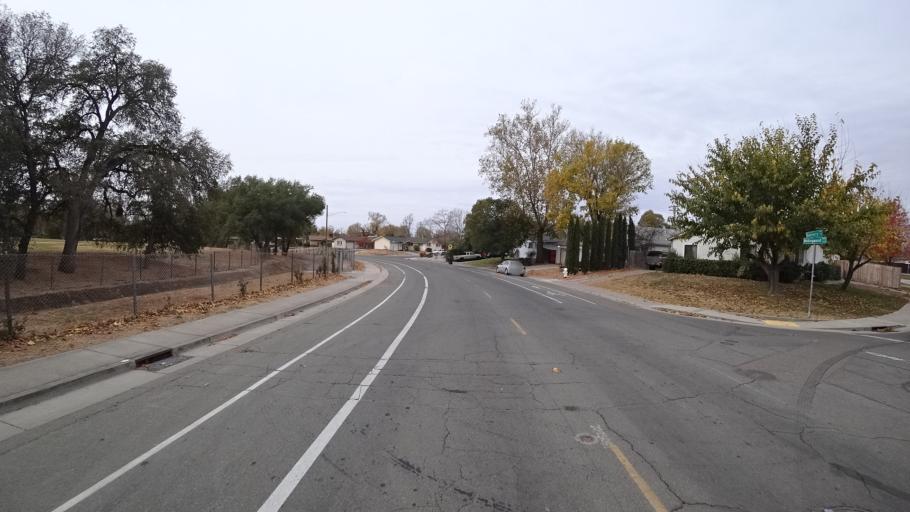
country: US
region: California
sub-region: Sacramento County
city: Citrus Heights
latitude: 38.7116
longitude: -121.3025
